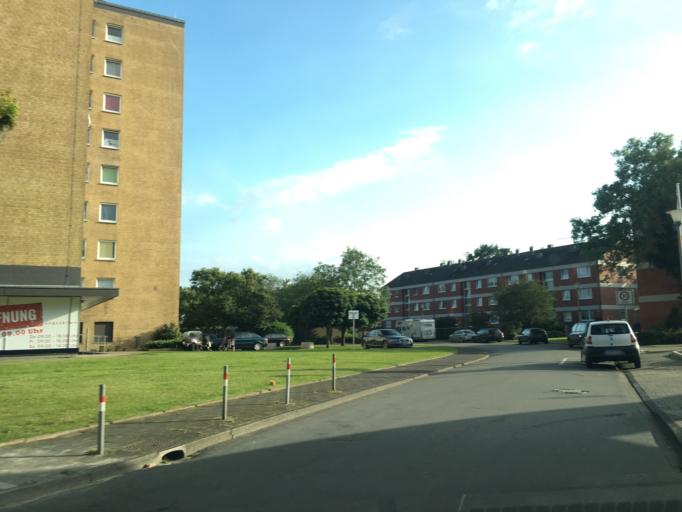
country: DE
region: North Rhine-Westphalia
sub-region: Regierungsbezirk Munster
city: Muenster
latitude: 51.9930
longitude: 7.6399
